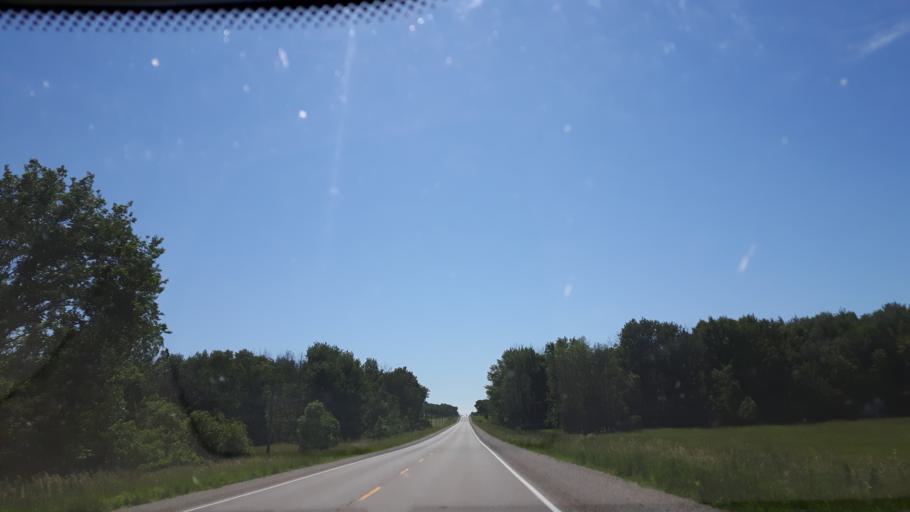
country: CA
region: Ontario
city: Bluewater
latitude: 43.4291
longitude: -81.5498
